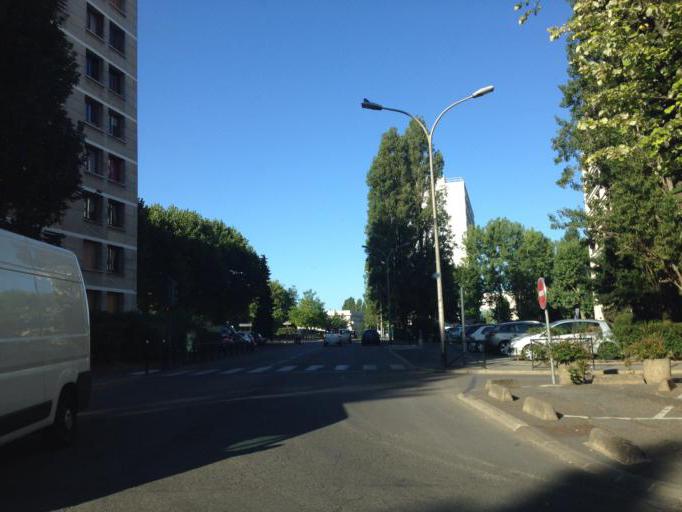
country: FR
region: Ile-de-France
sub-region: Departement des Hauts-de-Seine
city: Meudon
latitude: 48.7857
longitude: 2.2291
